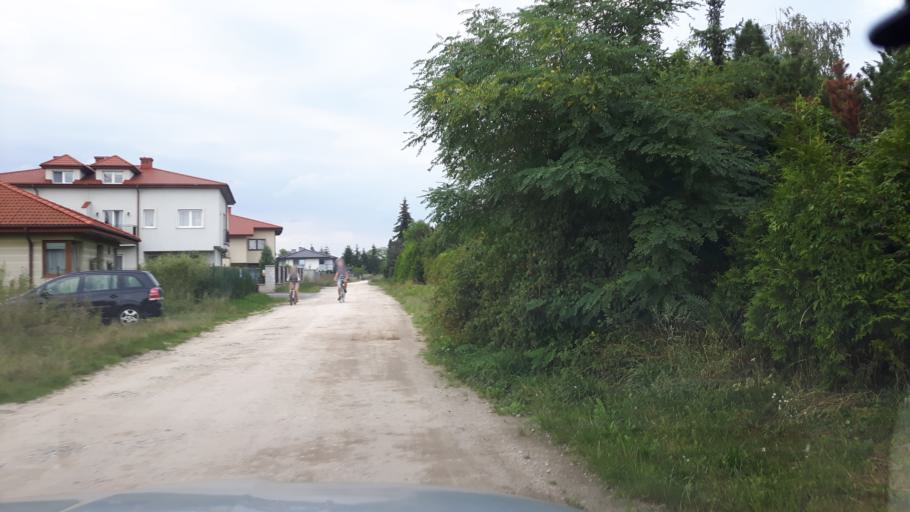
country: PL
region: Masovian Voivodeship
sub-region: Warszawa
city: Targowek
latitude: 52.3078
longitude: 21.0463
